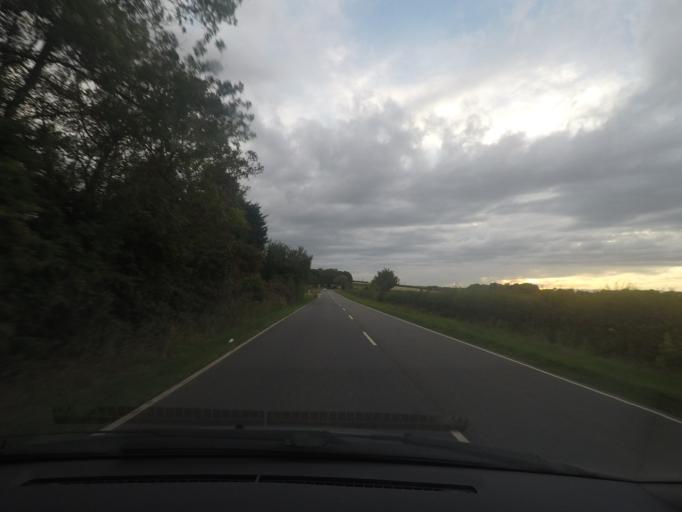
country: GB
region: England
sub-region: Lincolnshire
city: Holton le Clay
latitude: 53.4347
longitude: -0.0637
